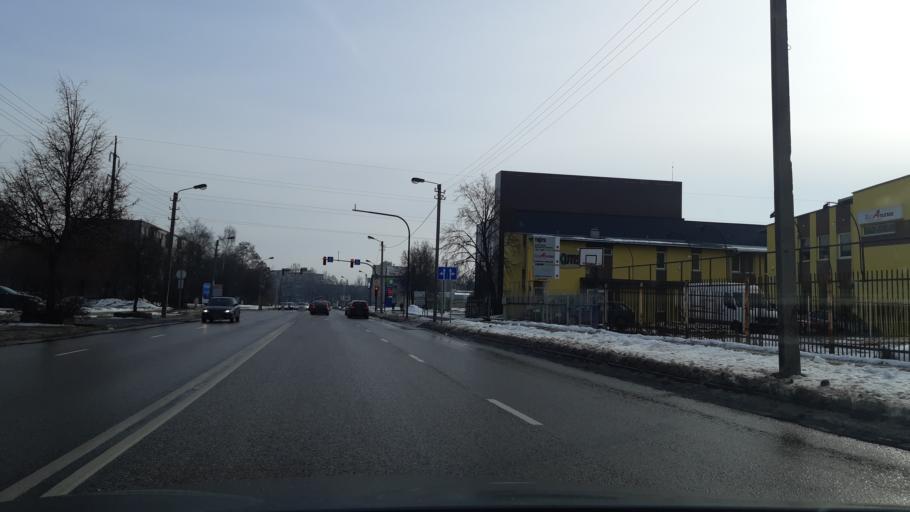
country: LT
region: Kauno apskritis
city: Dainava (Kaunas)
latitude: 54.9179
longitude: 23.9523
